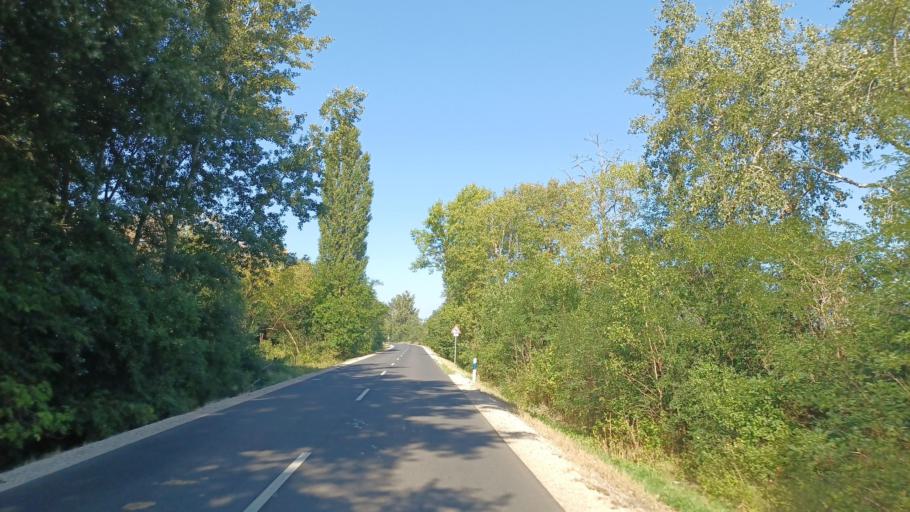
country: HU
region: Fejer
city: Alap
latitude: 46.7438
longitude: 18.6954
